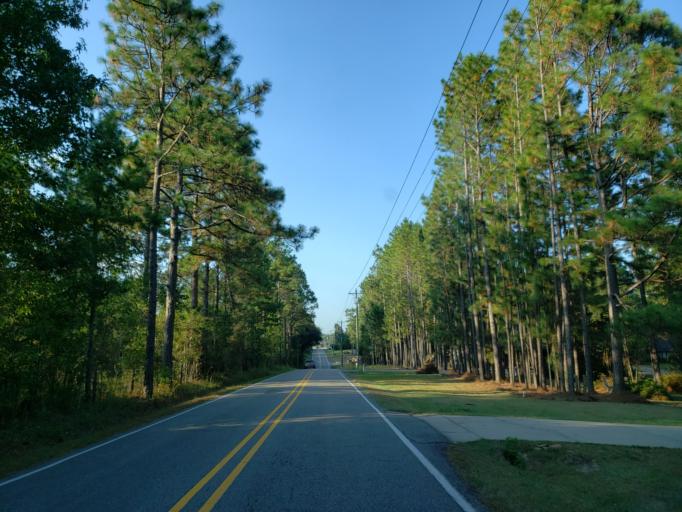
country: US
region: Mississippi
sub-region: Lamar County
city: West Hattiesburg
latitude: 31.3105
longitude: -89.4440
